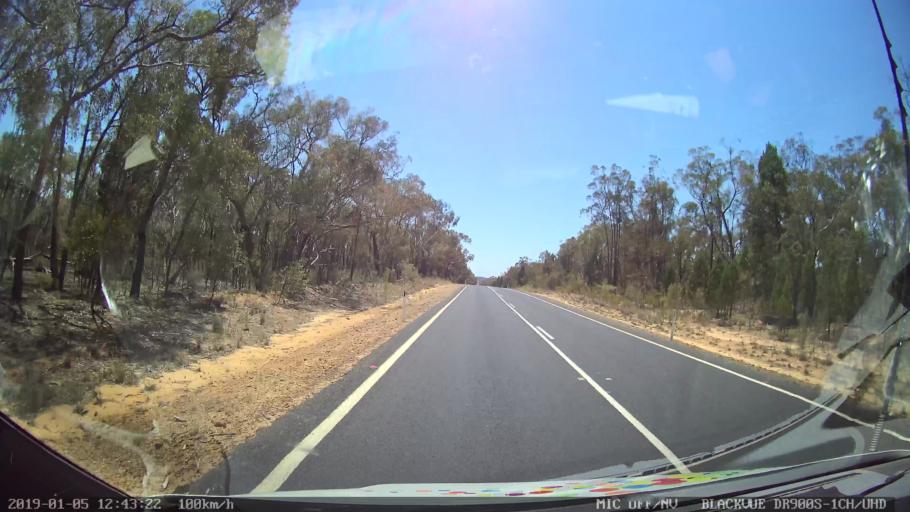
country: AU
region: New South Wales
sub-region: Warrumbungle Shire
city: Coonabarabran
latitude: -31.1488
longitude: 149.5231
